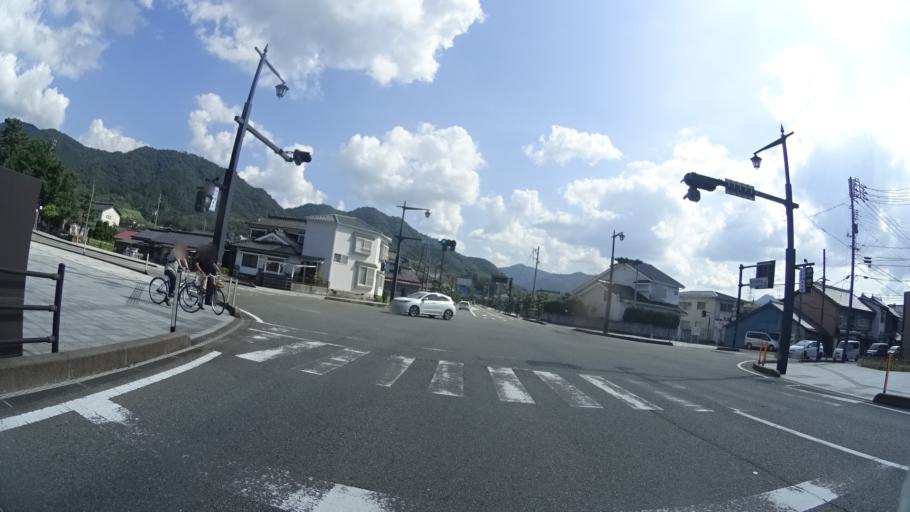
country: JP
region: Yamaguchi
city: Hagi
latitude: 34.4118
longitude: 131.4152
